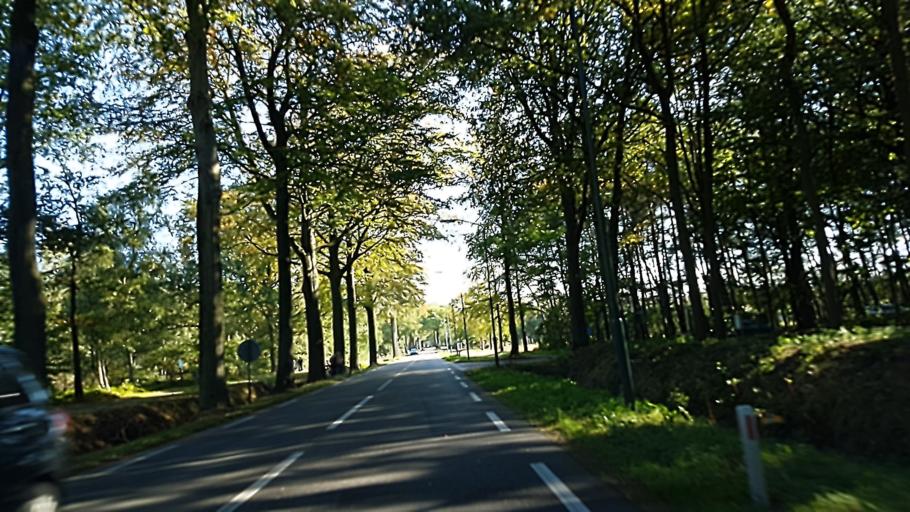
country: BE
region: Flanders
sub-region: Provincie Antwerpen
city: Stabroek
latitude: 51.3890
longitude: 4.3629
